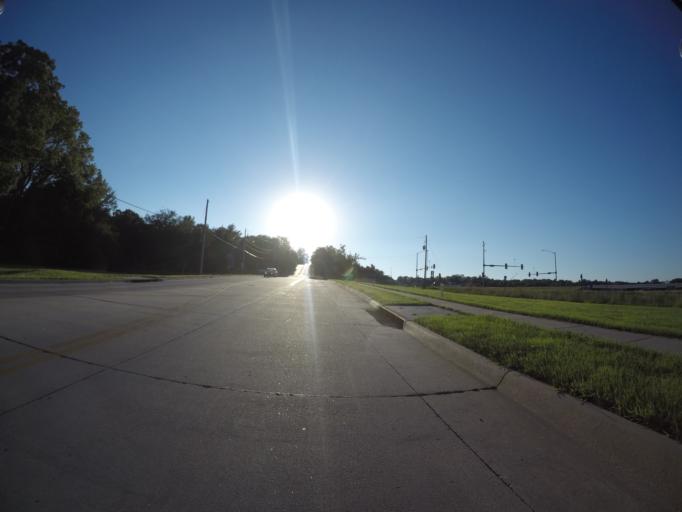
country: US
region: Kansas
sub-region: Riley County
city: Manhattan
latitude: 39.1674
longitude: -96.6029
